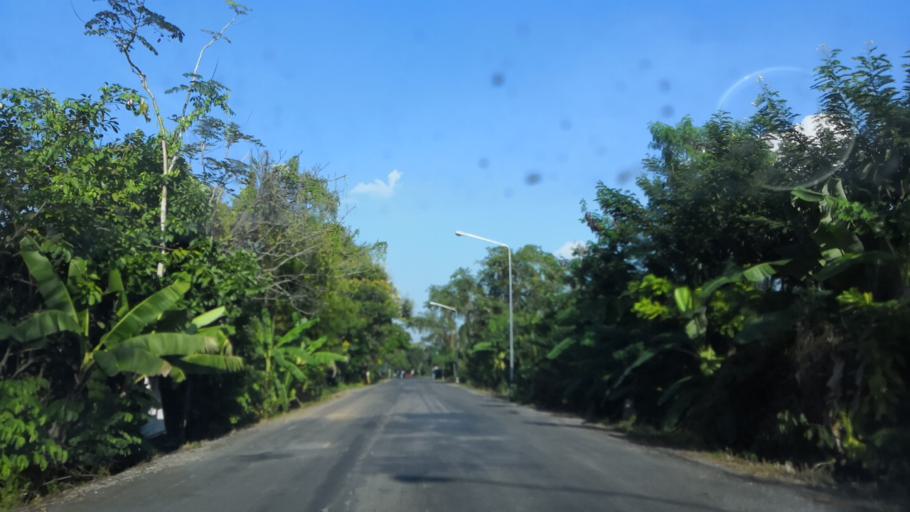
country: TH
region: Chiang Rai
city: Wiang Chai
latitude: 19.9605
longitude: 99.9434
